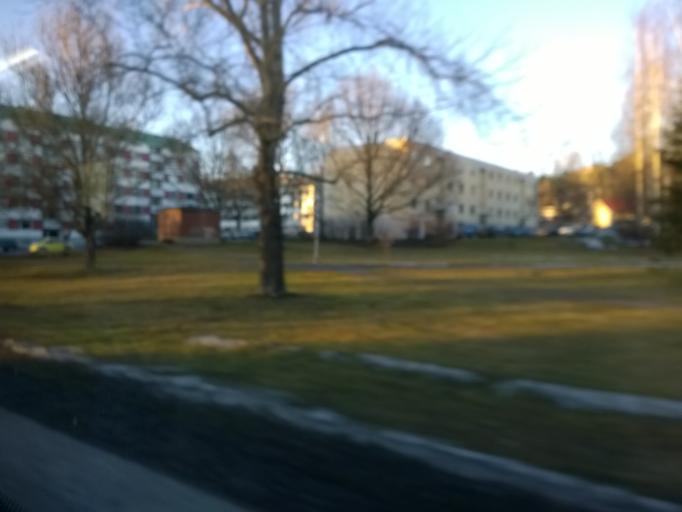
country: FI
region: Pirkanmaa
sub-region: Tampere
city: Tampere
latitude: 61.4888
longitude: 23.8013
